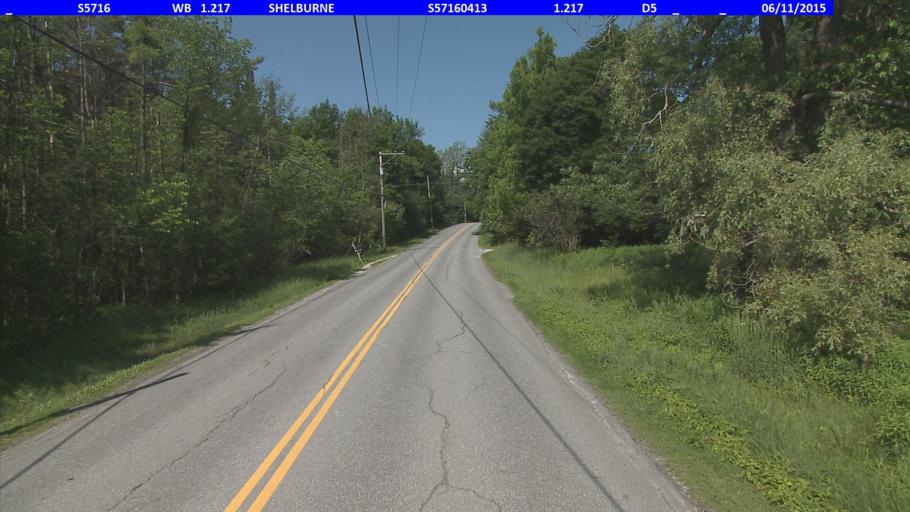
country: US
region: Vermont
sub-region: Chittenden County
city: Hinesburg
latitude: 44.3713
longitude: -73.1881
